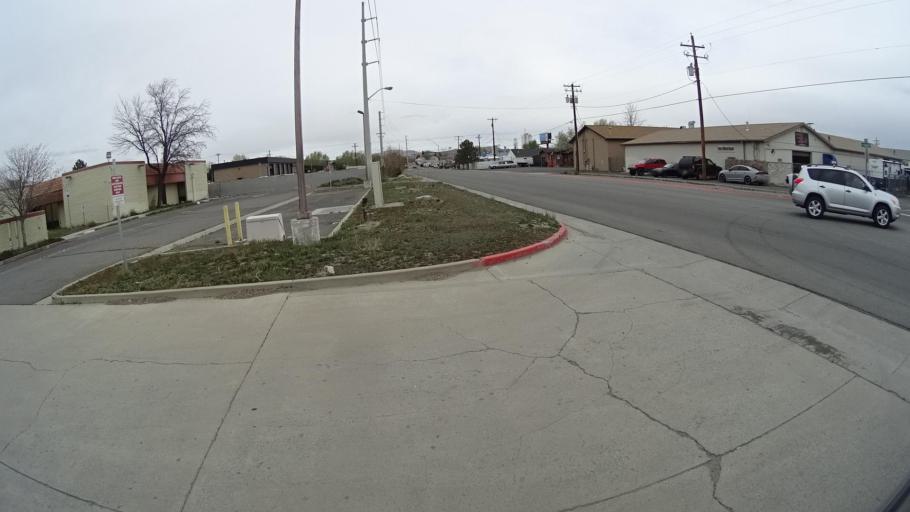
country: US
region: Nevada
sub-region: Washoe County
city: Sparks
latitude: 39.5259
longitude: -119.7716
